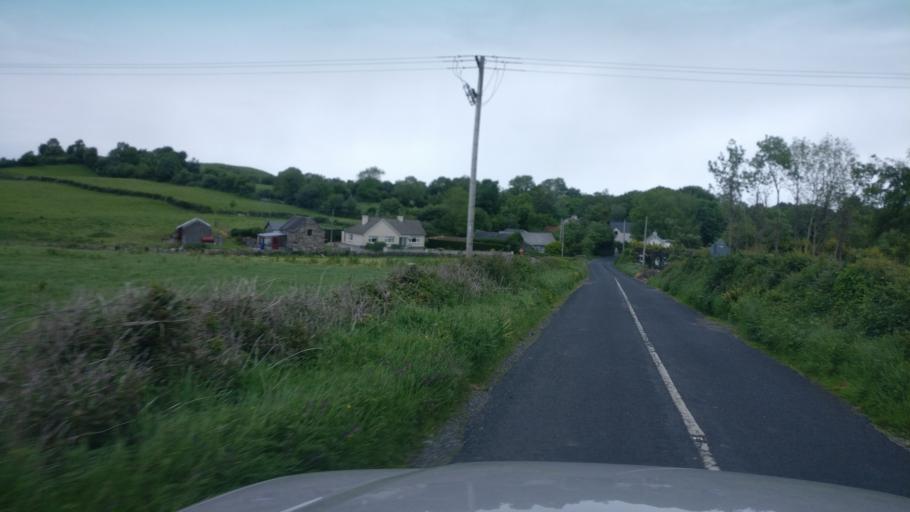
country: IE
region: Connaught
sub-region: County Galway
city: Loughrea
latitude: 53.1206
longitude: -8.4323
